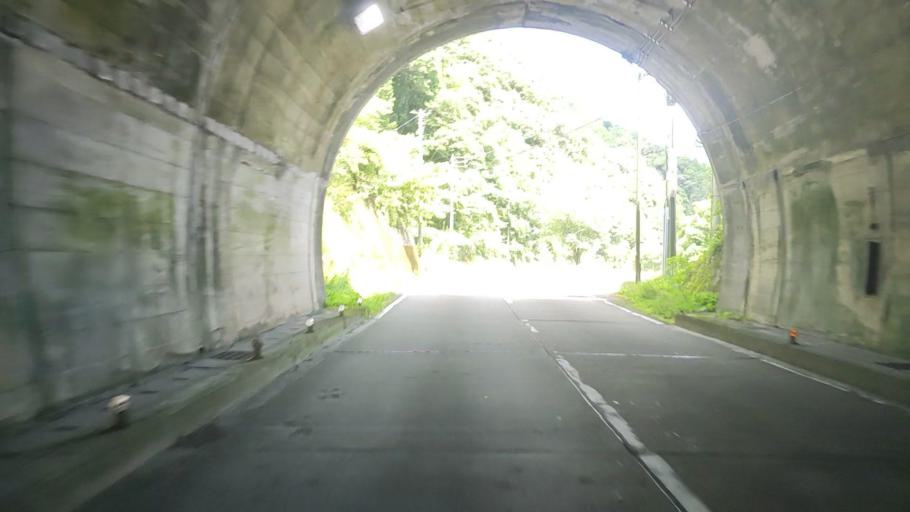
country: JP
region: Wakayama
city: Shingu
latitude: 33.7572
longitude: 135.9205
